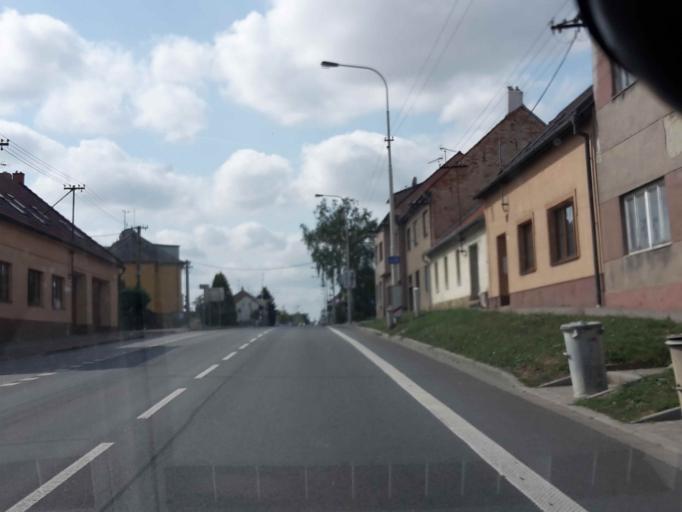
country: CZ
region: South Moravian
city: Rousinov
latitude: 49.2011
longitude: 16.8754
